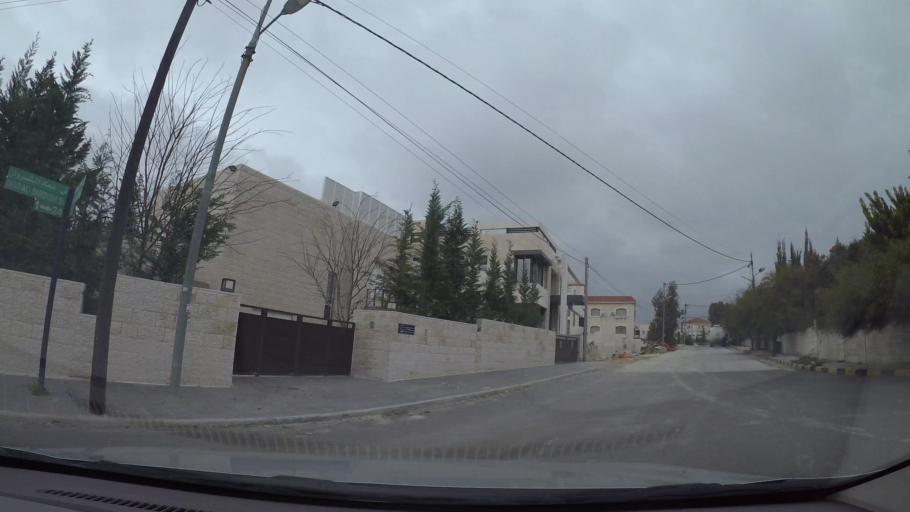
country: JO
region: Amman
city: Wadi as Sir
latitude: 31.9924
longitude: 35.8342
